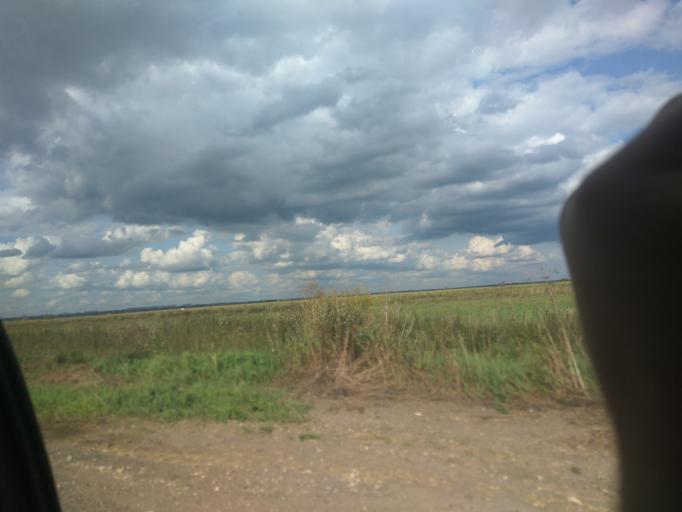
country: RU
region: Moskovskaya
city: Ramenskoye
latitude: 55.5057
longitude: 38.2232
